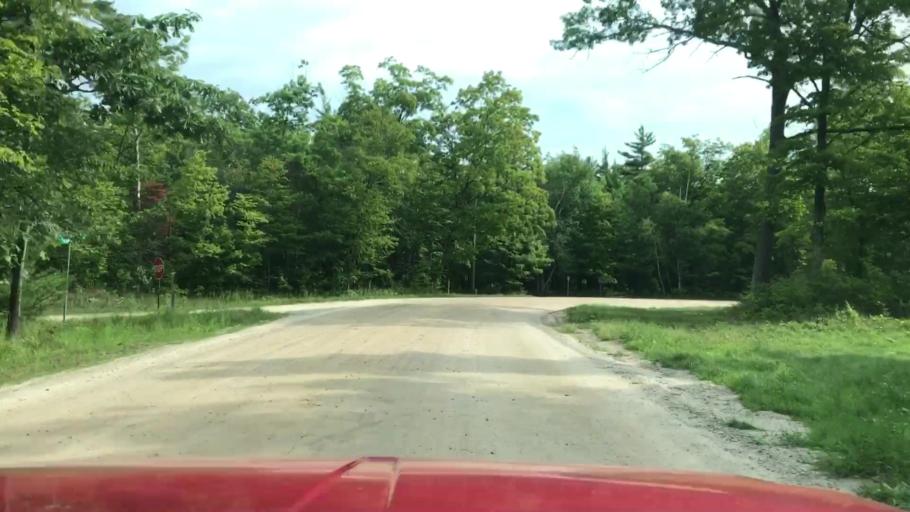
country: US
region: Michigan
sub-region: Charlevoix County
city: Charlevoix
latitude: 45.7480
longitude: -85.5389
